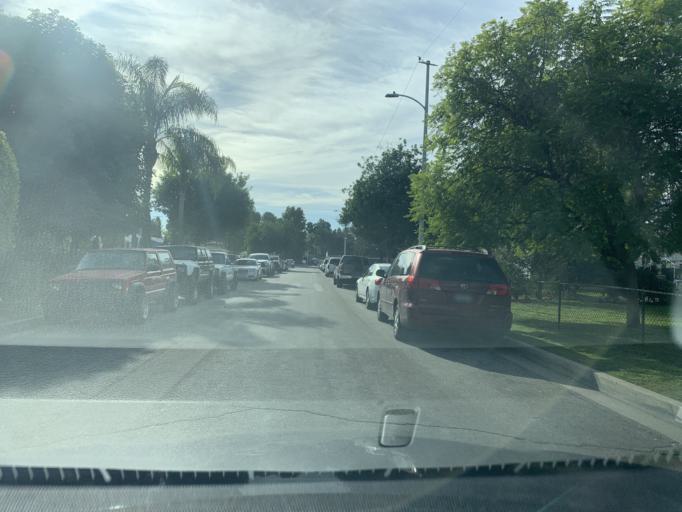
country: US
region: California
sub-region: Los Angeles County
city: West Covina
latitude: 34.0747
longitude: -117.9405
